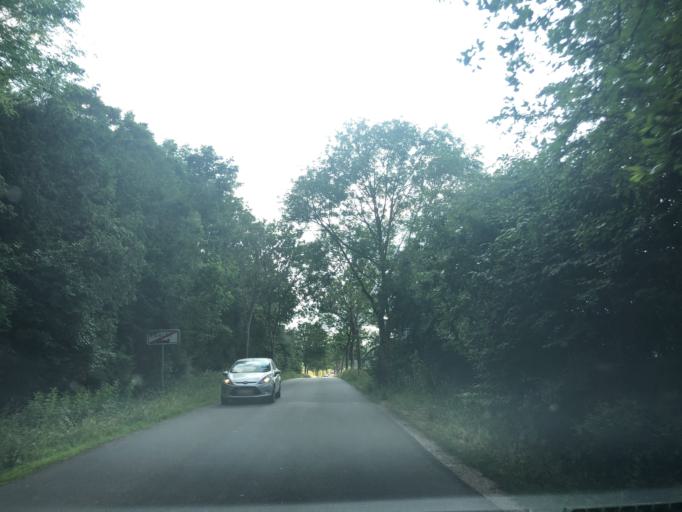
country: DK
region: Zealand
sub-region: Faxe Kommune
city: Ronnede
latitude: 55.3081
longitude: 12.0448
